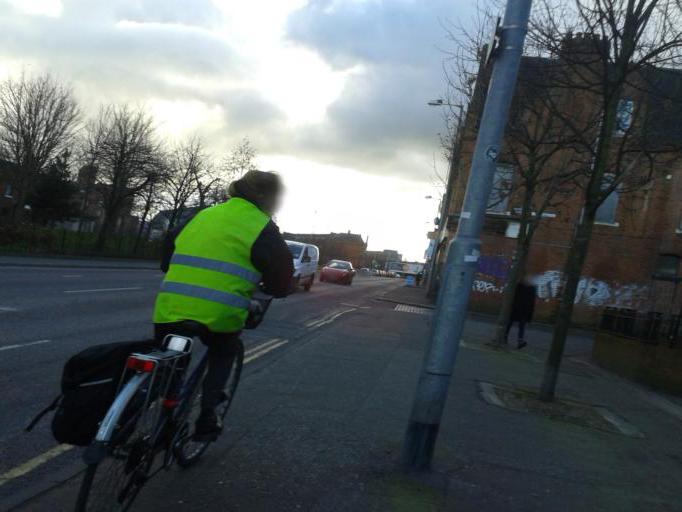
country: GB
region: Northern Ireland
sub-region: City of Belfast
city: Belfast
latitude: 54.5937
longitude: -5.9249
